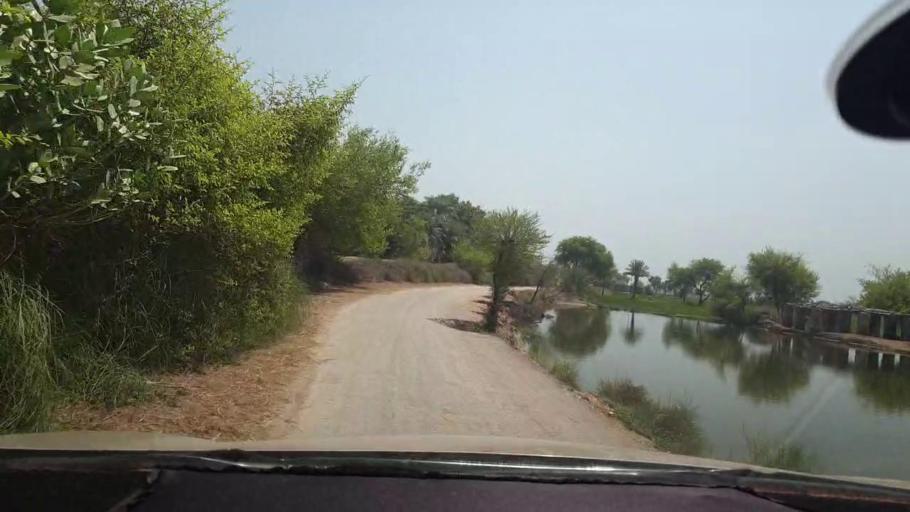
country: PK
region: Sindh
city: Kambar
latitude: 27.6605
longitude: 67.9324
